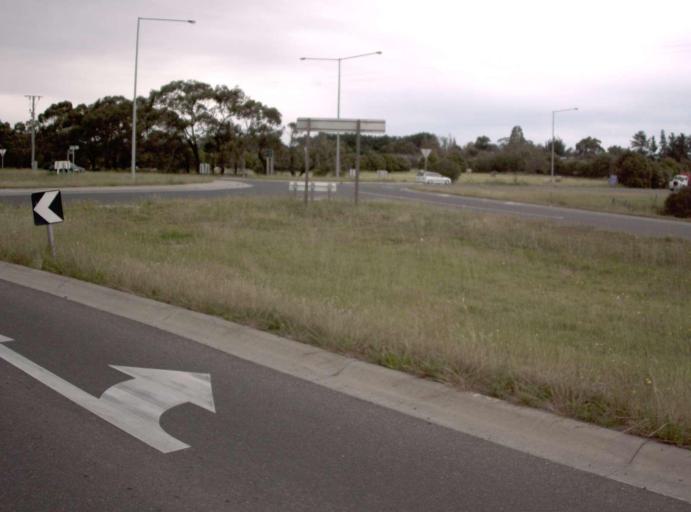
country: AU
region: Victoria
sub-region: Casey
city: Blind Bight
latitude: -38.1924
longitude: 145.3505
